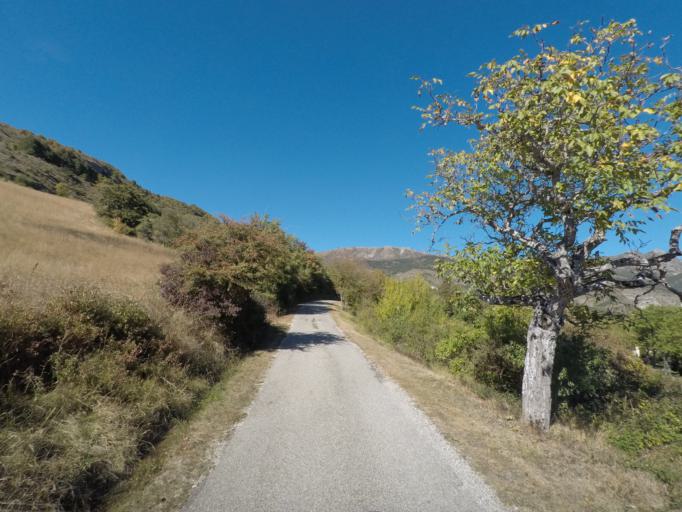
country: FR
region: Provence-Alpes-Cote d'Azur
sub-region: Departement des Hautes-Alpes
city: Serres
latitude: 44.3979
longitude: 5.5022
